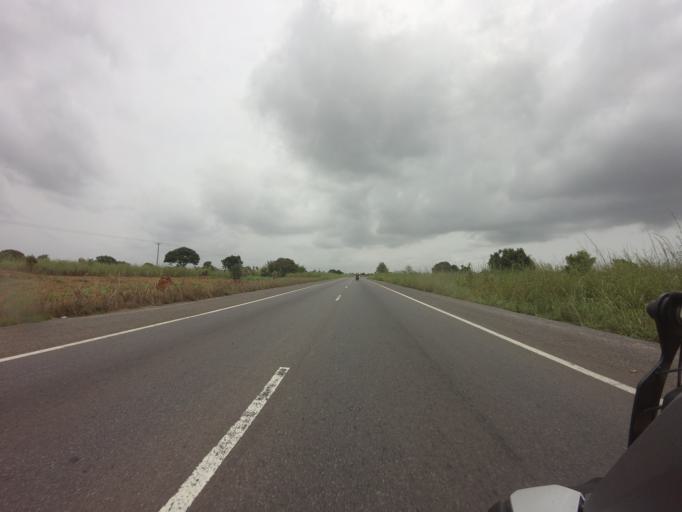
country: GH
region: Volta
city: Keta
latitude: 6.0653
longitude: 0.8792
